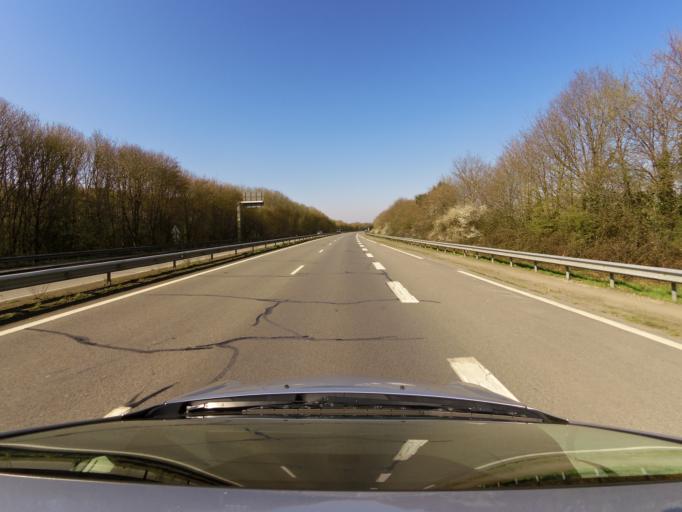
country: FR
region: Brittany
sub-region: Departement d'Ille-et-Vilaine
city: Mordelles
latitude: 48.0672
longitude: -1.8256
